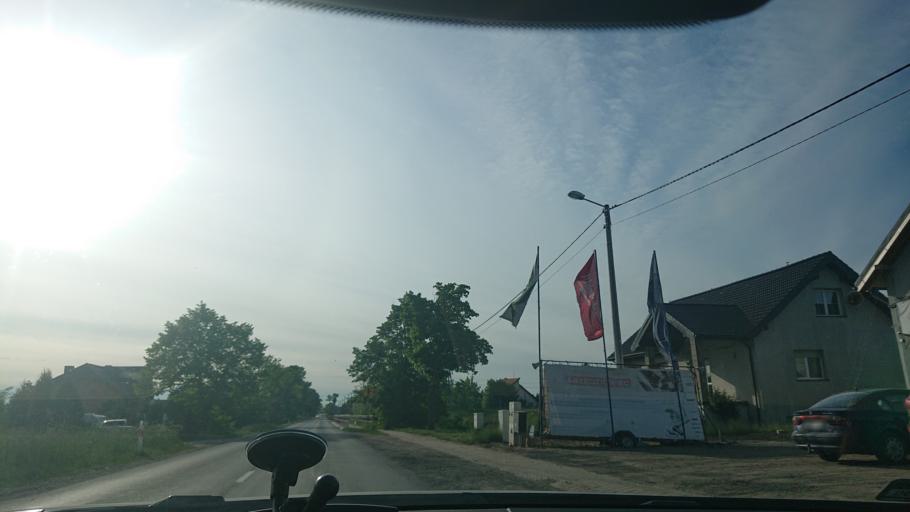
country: PL
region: Greater Poland Voivodeship
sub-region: Powiat gnieznienski
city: Gniezno
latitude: 52.5500
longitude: 17.5553
